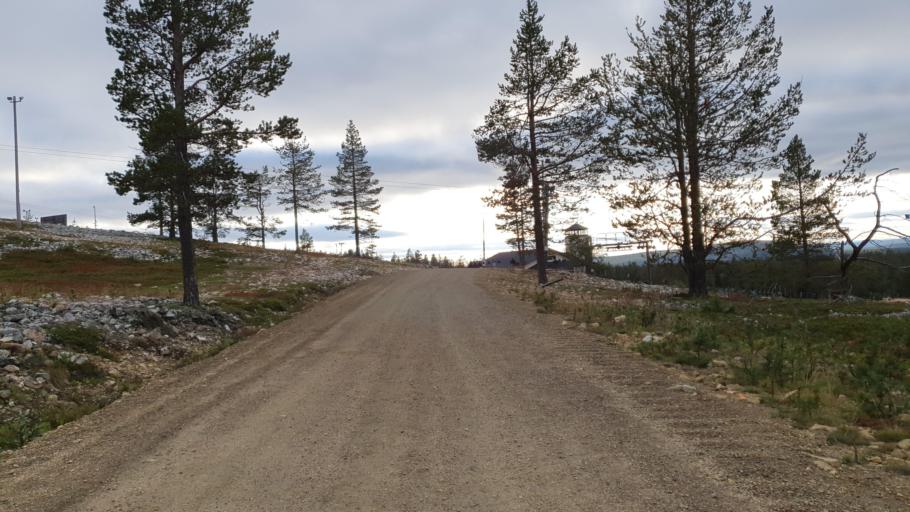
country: FI
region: Lapland
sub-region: Tunturi-Lappi
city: Kolari
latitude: 67.5796
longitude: 24.2092
